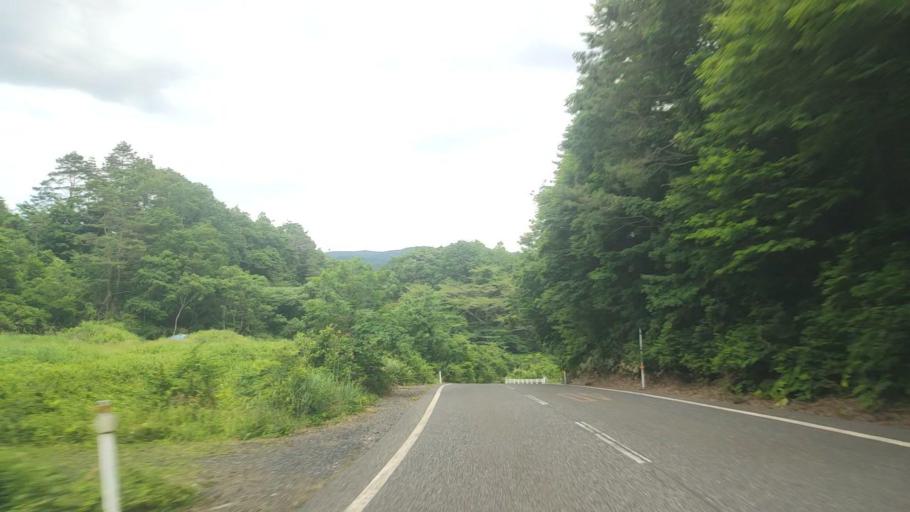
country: JP
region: Tottori
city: Kurayoshi
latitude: 35.2925
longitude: 133.9913
